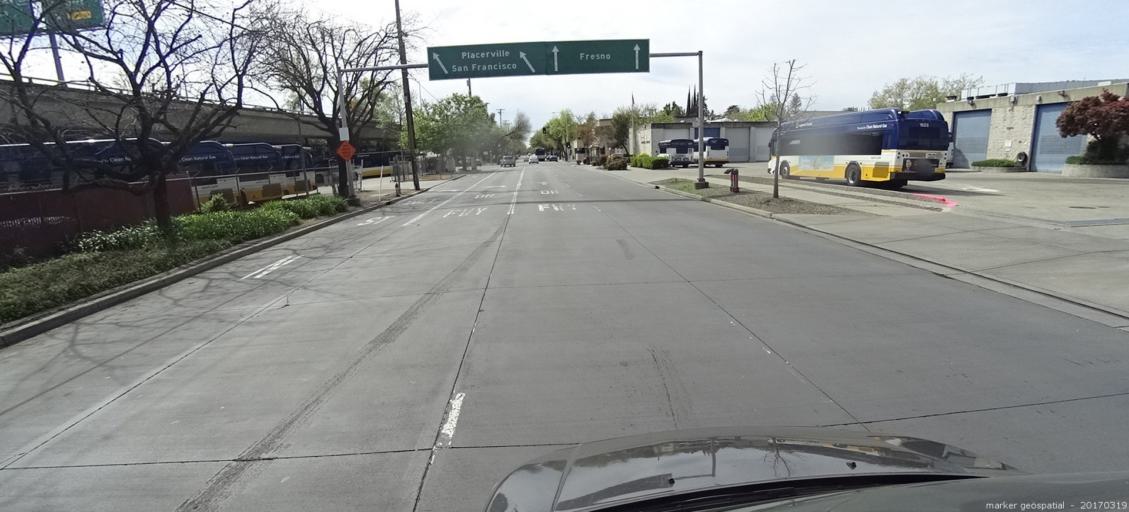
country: US
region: California
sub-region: Sacramento County
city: Sacramento
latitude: 38.5700
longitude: -121.4695
